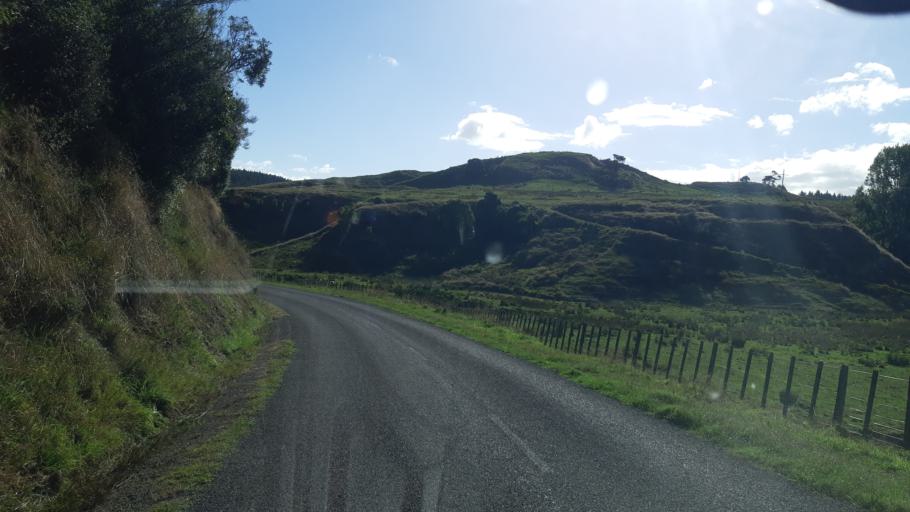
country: NZ
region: Manawatu-Wanganui
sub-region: Rangitikei District
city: Bulls
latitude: -39.9008
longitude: 175.3393
